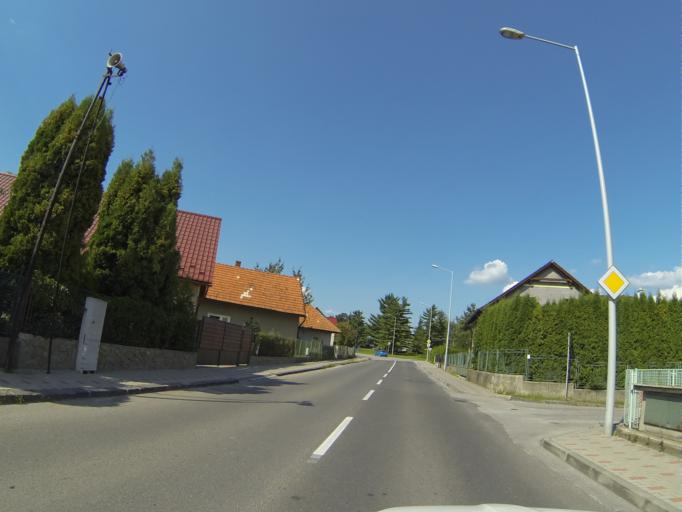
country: SK
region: Nitriansky
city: Bojnice
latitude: 48.7904
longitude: 18.5869
